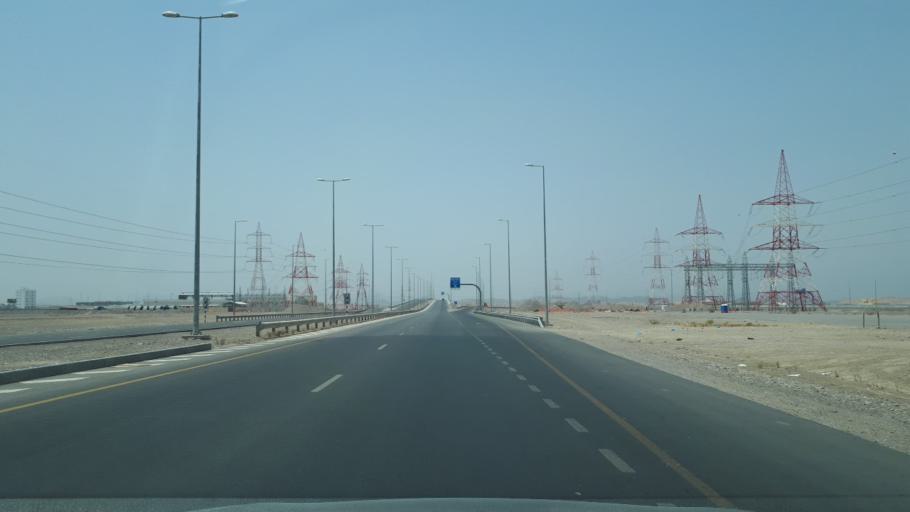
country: OM
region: Muhafazat Masqat
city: As Sib al Jadidah
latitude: 23.6146
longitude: 58.0915
